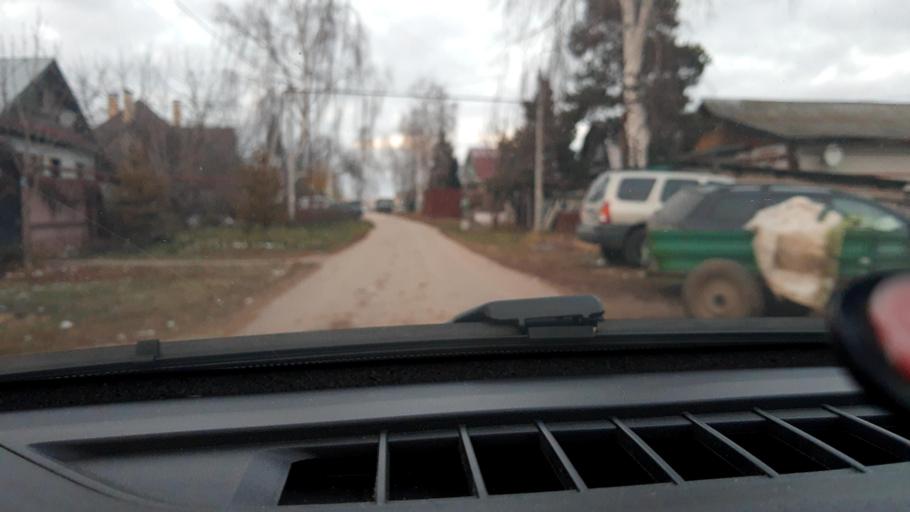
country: RU
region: Nizjnij Novgorod
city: Afonino
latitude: 56.2383
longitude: 44.1061
